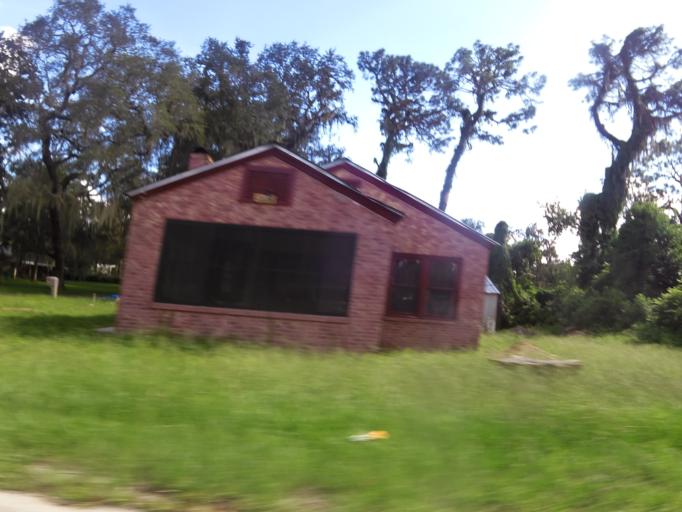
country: US
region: Florida
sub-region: Putnam County
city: Palatka
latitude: 29.6433
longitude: -81.6490
